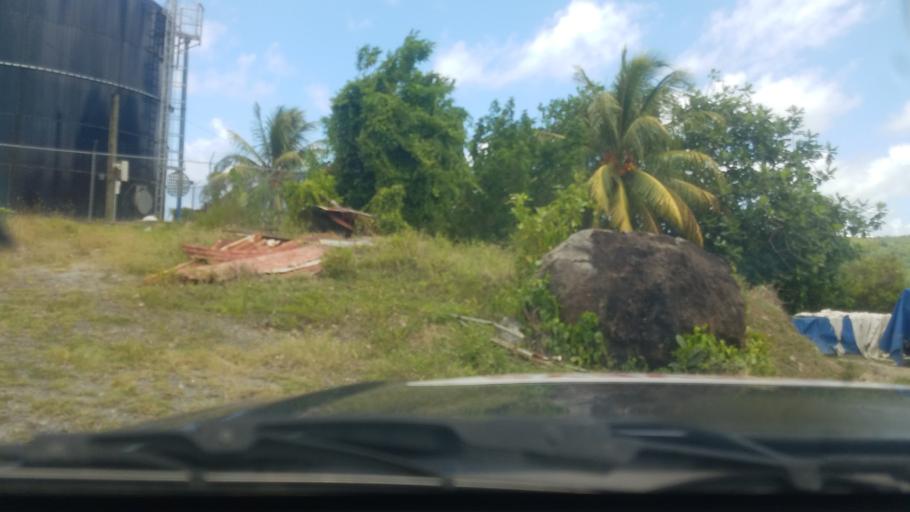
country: LC
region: Dennery Quarter
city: Dennery
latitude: 13.9176
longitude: -60.8934
